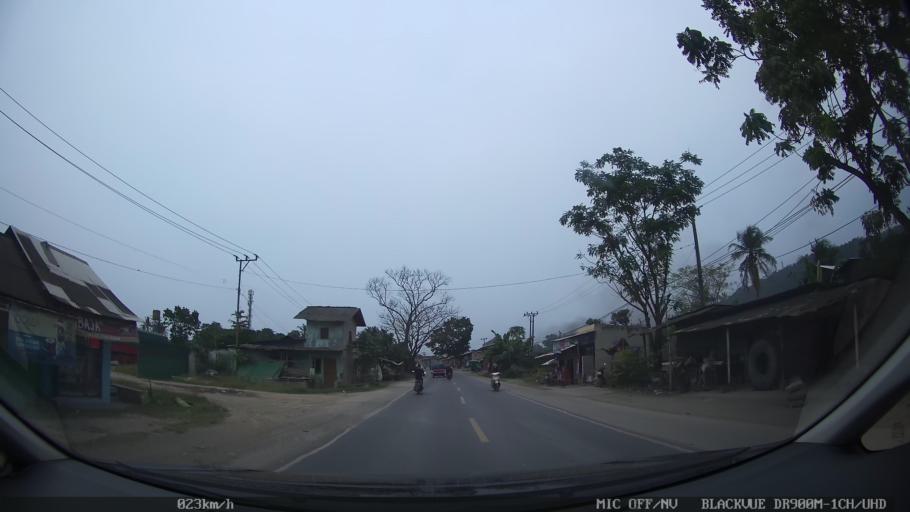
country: ID
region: Lampung
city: Panjang
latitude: -5.4298
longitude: 105.3268
